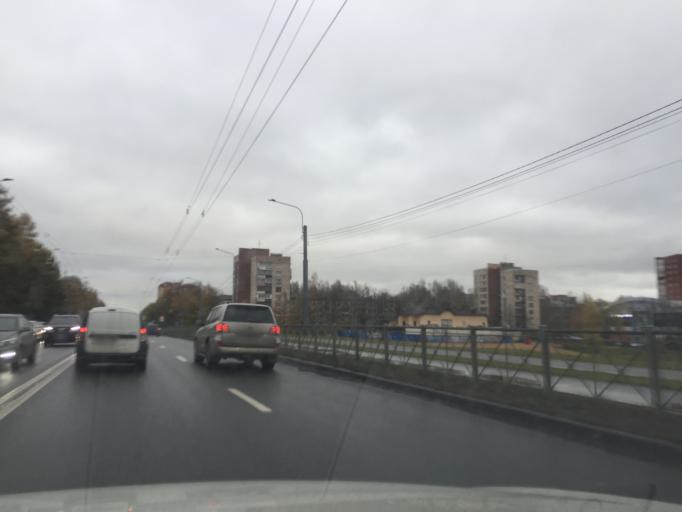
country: RU
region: St.-Petersburg
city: Sosnovka
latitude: 60.0141
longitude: 30.3563
